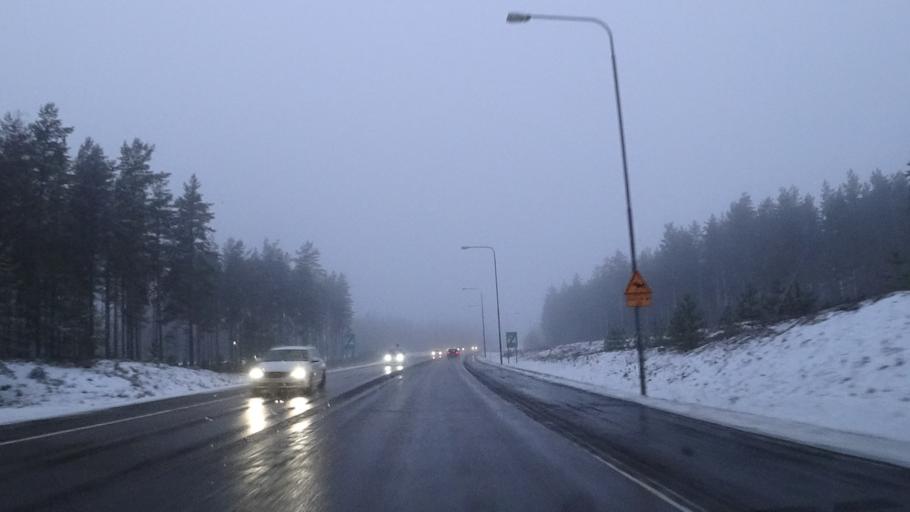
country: FI
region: Paijanne Tavastia
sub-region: Lahti
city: Hollola
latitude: 60.9834
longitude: 25.4189
